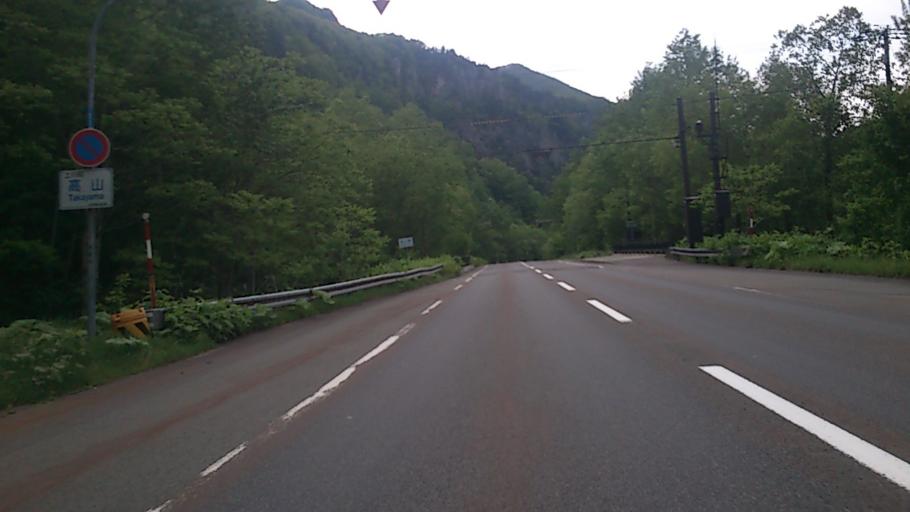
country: JP
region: Hokkaido
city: Kamikawa
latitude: 43.7546
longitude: 142.9281
